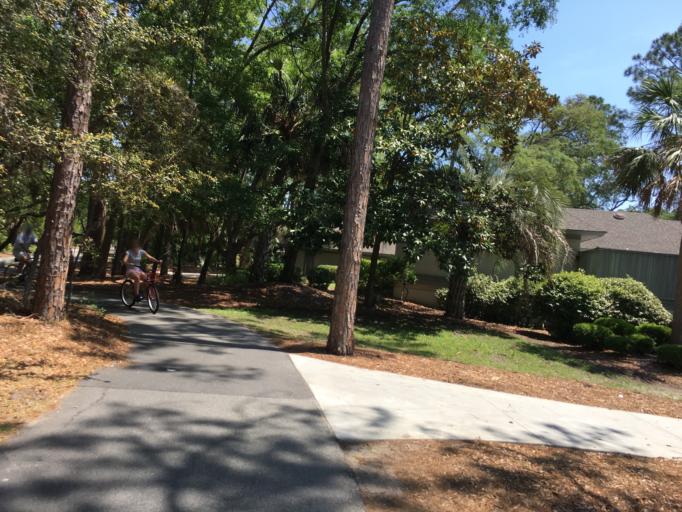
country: US
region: Georgia
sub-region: Chatham County
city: Tybee Island
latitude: 32.1106
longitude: -80.8217
